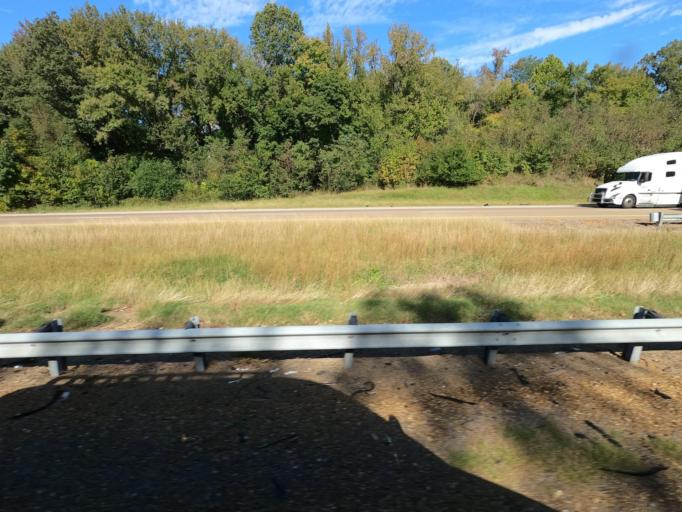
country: US
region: Tennessee
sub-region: Shelby County
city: Arlington
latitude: 35.2709
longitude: -89.6484
